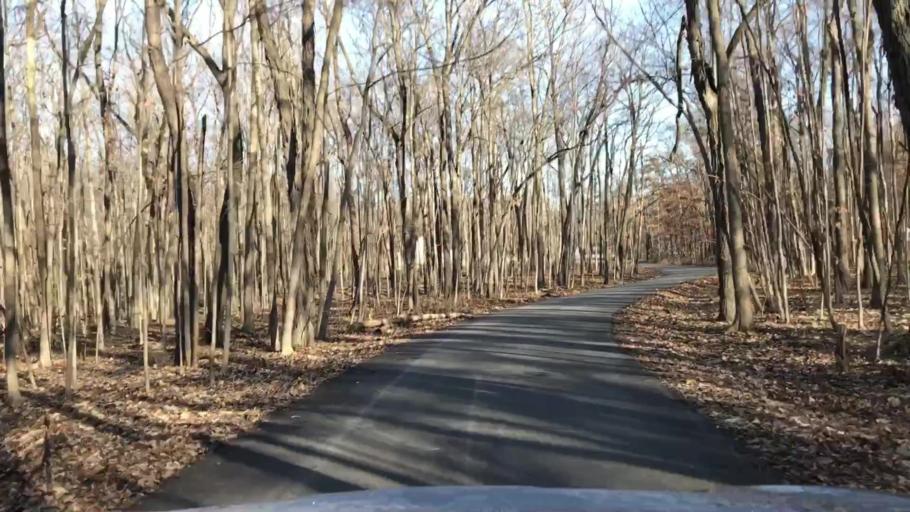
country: US
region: Illinois
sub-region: McLean County
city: Hudson
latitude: 40.6476
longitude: -88.9149
